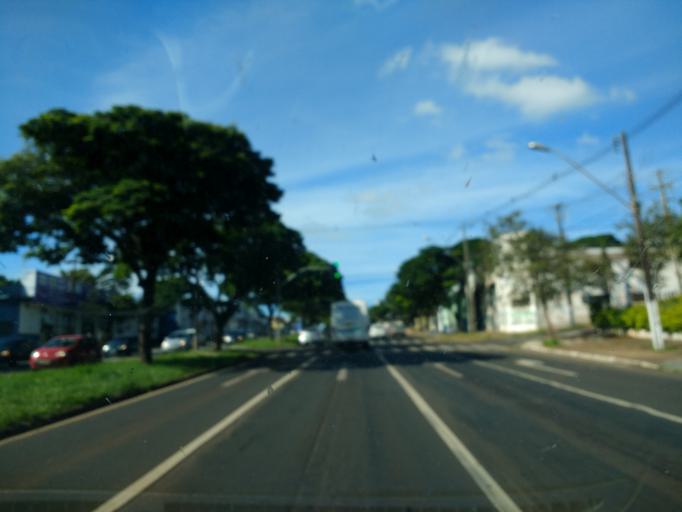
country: BR
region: Parana
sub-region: Maringa
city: Maringa
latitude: -23.4179
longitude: -51.9604
